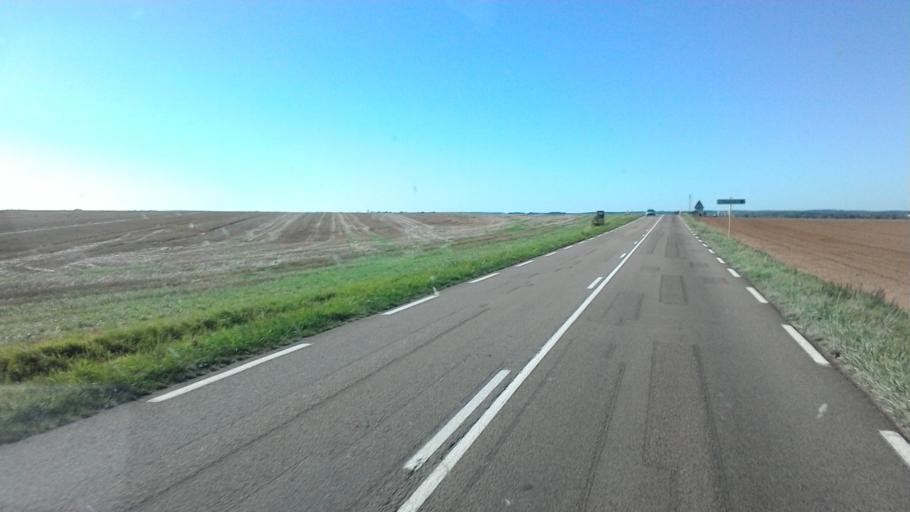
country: FR
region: Bourgogne
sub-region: Departement de la Cote-d'Or
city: Chatillon-sur-Seine
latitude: 47.8827
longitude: 4.5945
